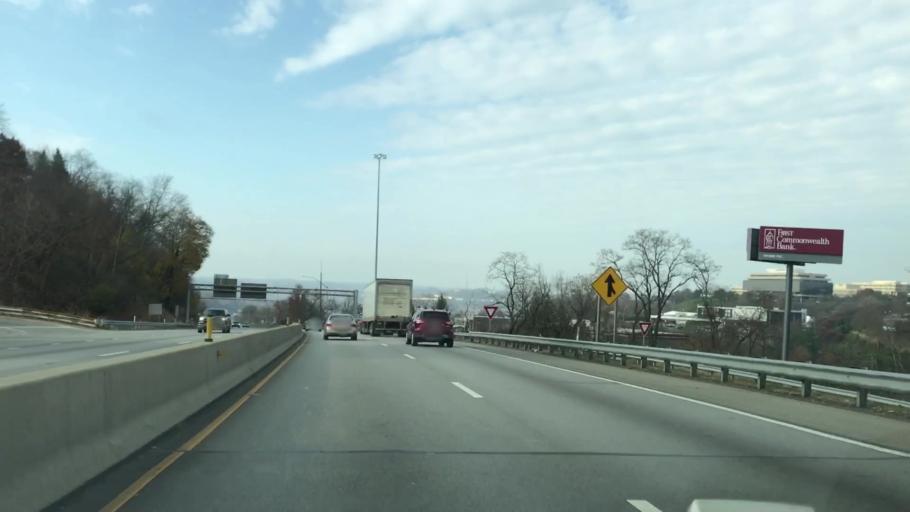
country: US
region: Pennsylvania
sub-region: Allegheny County
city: Green Tree
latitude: 40.4198
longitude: -80.0499
